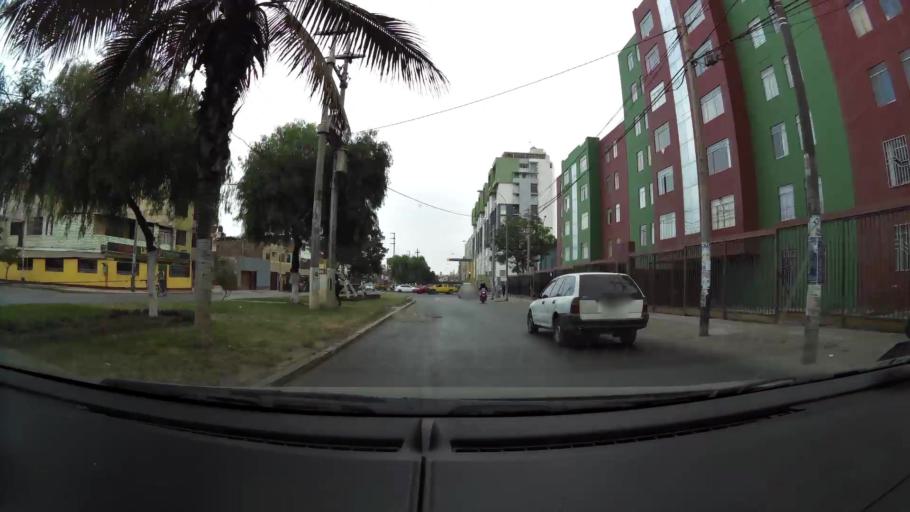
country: PE
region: La Libertad
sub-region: Provincia de Trujillo
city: Trujillo
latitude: -8.0954
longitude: -79.0277
